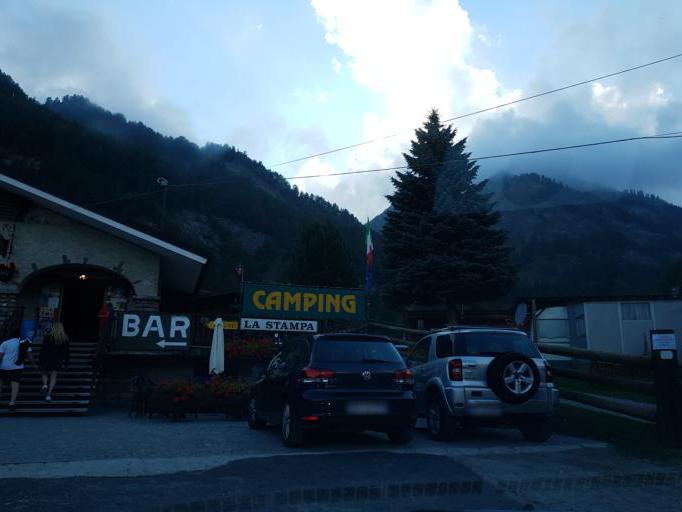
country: IT
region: Piedmont
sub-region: Provincia di Cuneo
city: Pontechianale
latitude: 44.6209
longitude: 7.0277
